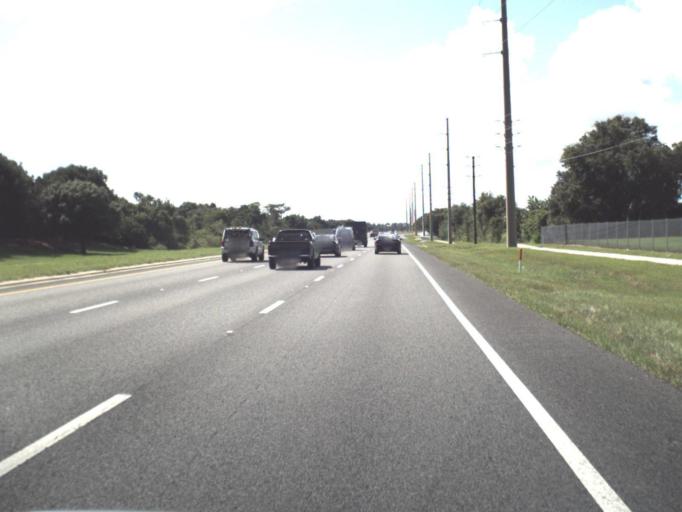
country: US
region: Florida
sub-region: Sarasota County
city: The Meadows
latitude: 27.4321
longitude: -82.4067
